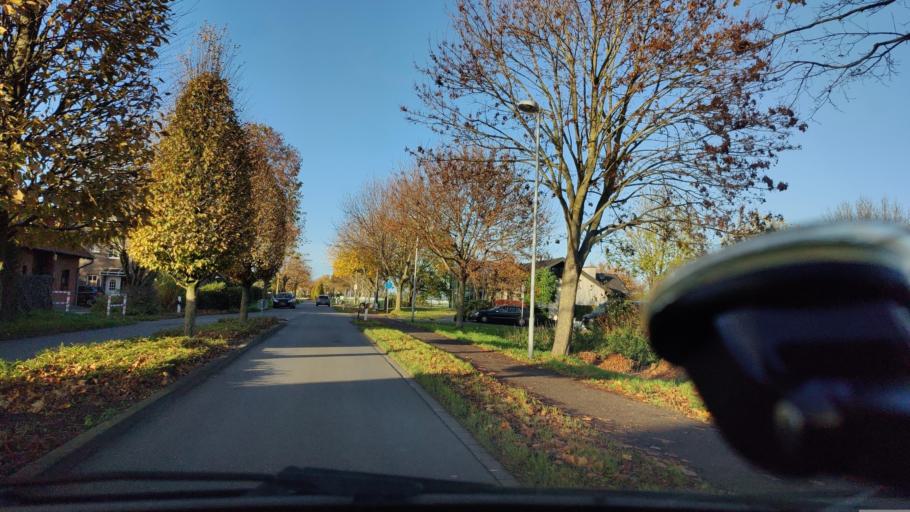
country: DE
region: North Rhine-Westphalia
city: Straelen
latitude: 51.4505
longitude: 6.2660
